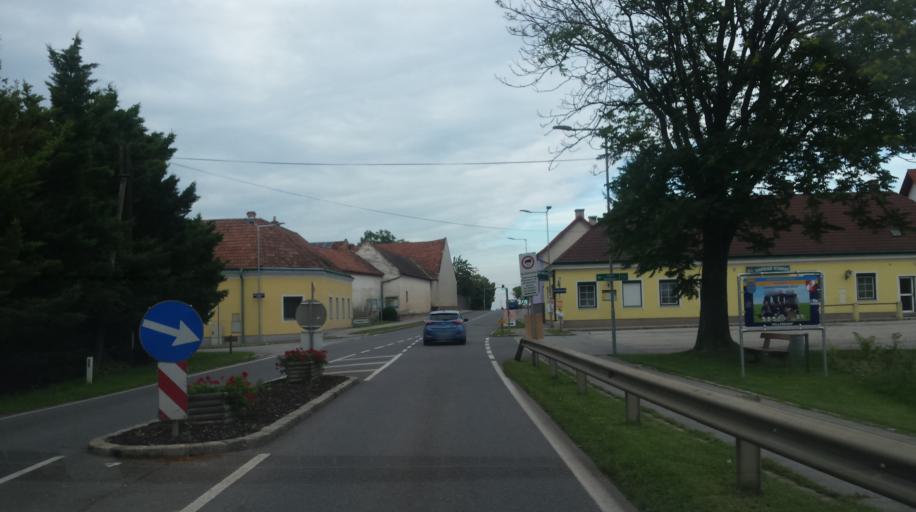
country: AT
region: Lower Austria
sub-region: Politischer Bezirk Wien-Umgebung
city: Zwolfaxing
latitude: 48.0971
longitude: 16.4541
